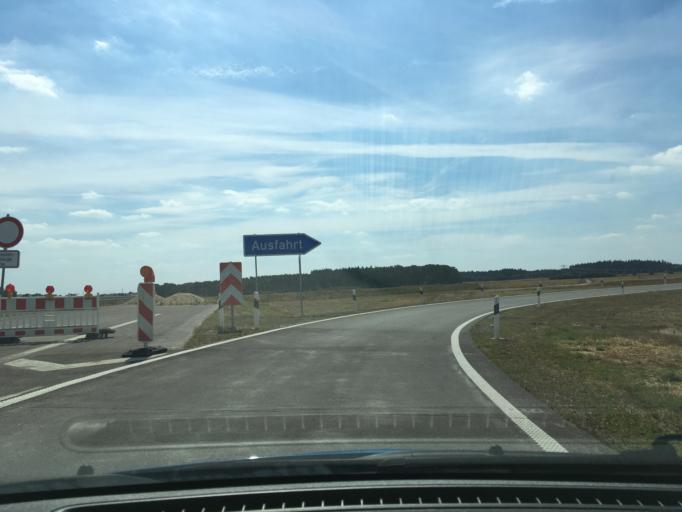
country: DE
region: Brandenburg
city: Karstadt
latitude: 53.1550
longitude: 11.7319
